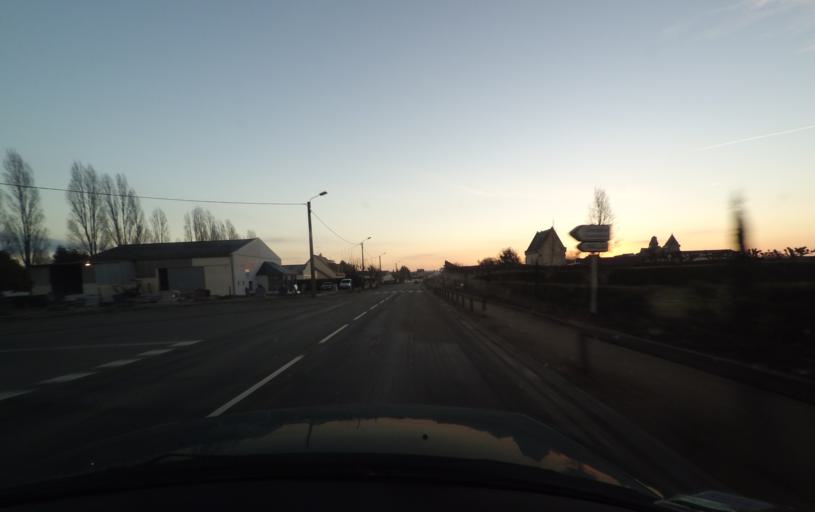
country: FR
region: Pays de la Loire
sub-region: Departement de la Mayenne
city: Evron
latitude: 48.1588
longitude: -0.4083
